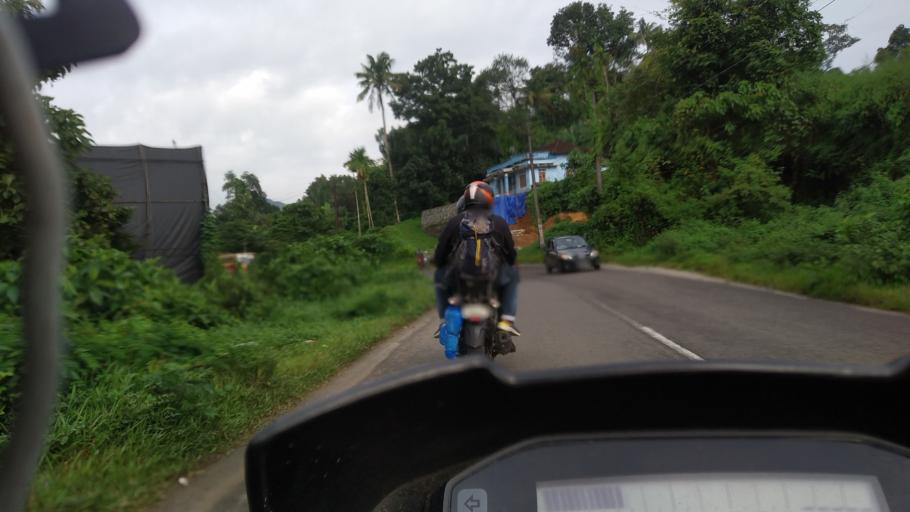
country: IN
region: Kerala
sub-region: Idukki
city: Kuttampuzha
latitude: 10.0520
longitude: 76.7396
